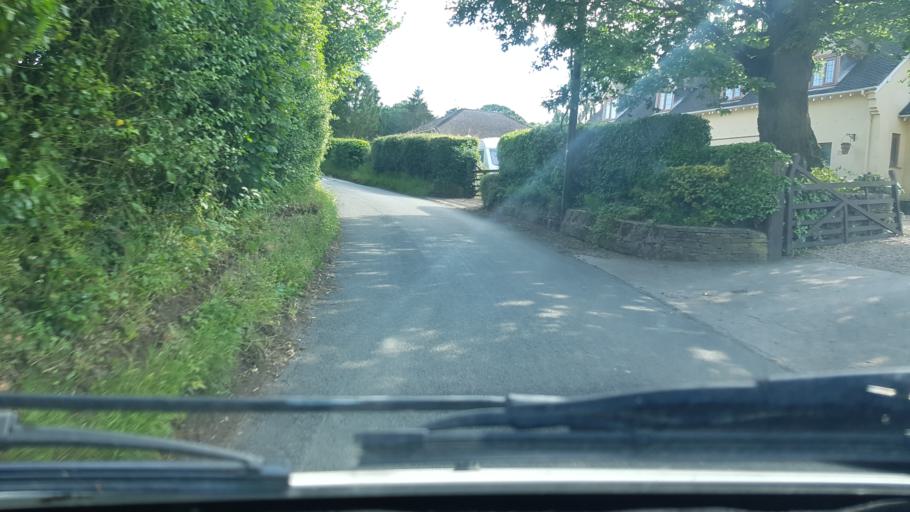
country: GB
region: England
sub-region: Worcestershire
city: Bewdley
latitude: 52.3644
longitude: -2.3246
